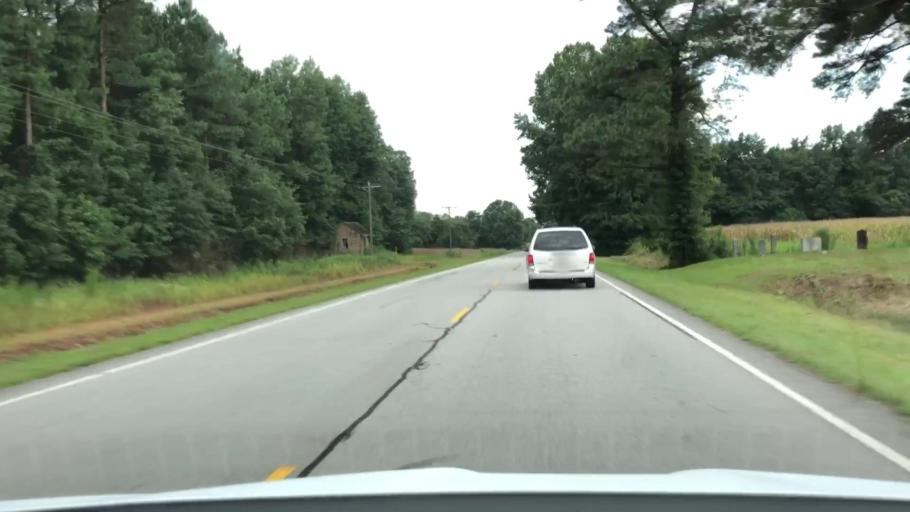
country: US
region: North Carolina
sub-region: Jones County
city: Trenton
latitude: 35.0787
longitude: -77.4094
